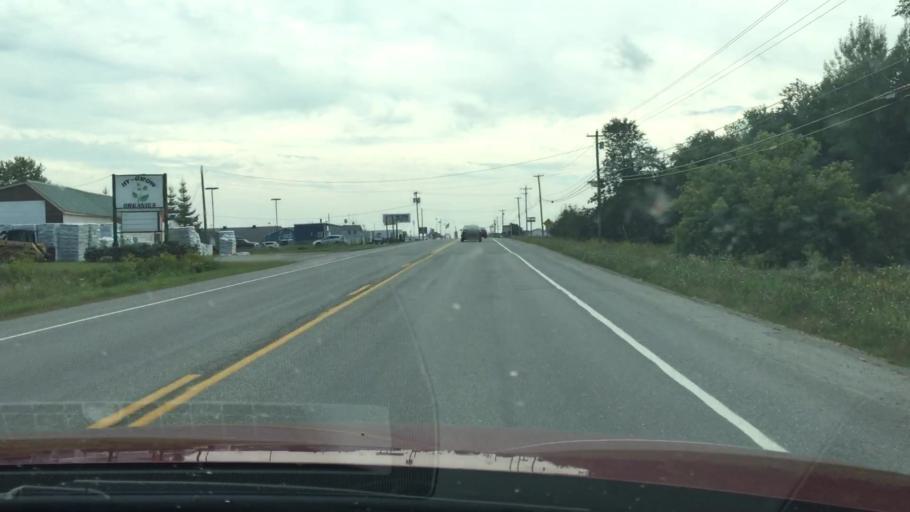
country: US
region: Maine
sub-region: Aroostook County
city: Houlton
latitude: 46.1502
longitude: -67.8405
